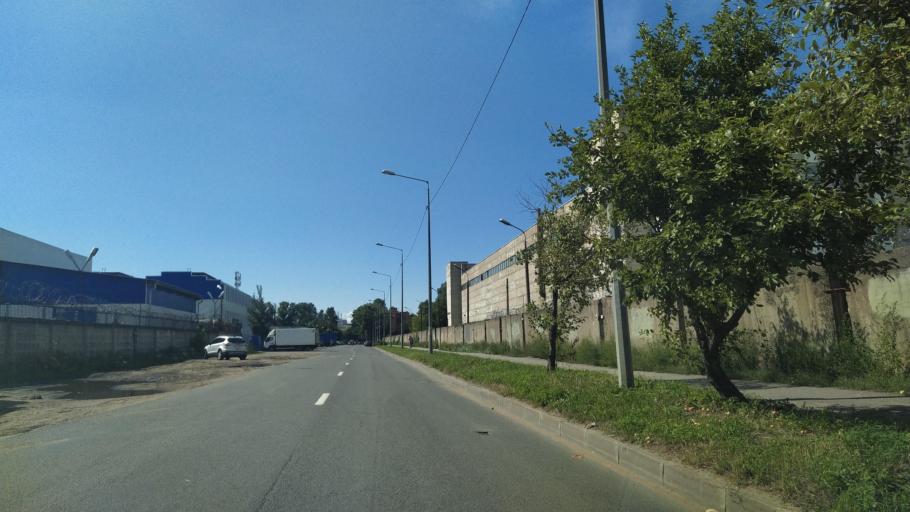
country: RU
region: Leningrad
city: Finlyandskiy
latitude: 59.9752
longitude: 30.3583
